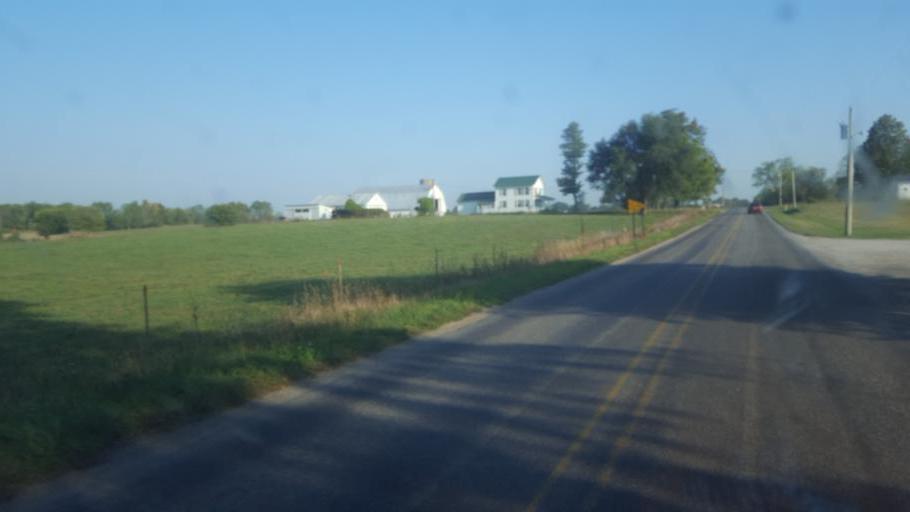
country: US
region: Indiana
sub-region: LaGrange County
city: Lagrange
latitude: 41.6271
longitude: -85.4246
